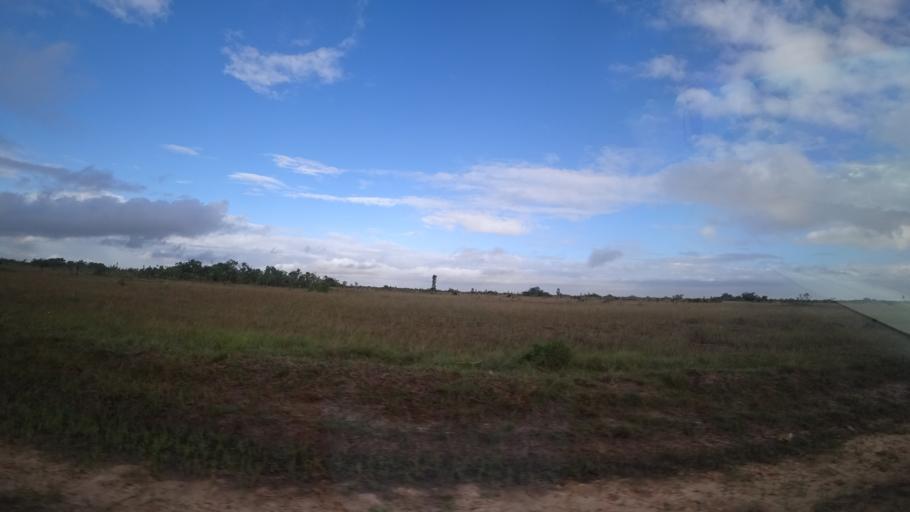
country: MZ
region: Sofala
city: Beira
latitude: -19.6773
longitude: 35.0595
